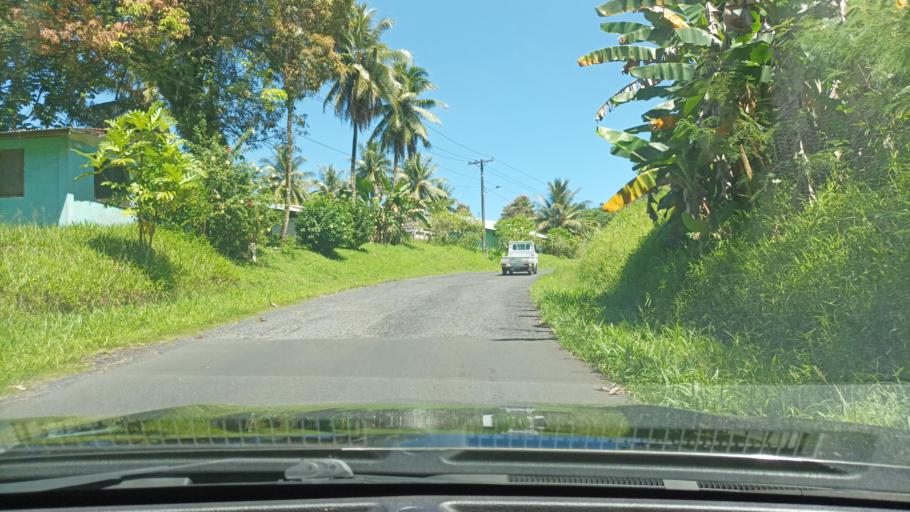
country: FM
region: Pohnpei
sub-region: Madolenihm Municipality
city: Madolenihm Municipality Government
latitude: 6.9194
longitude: 158.3227
